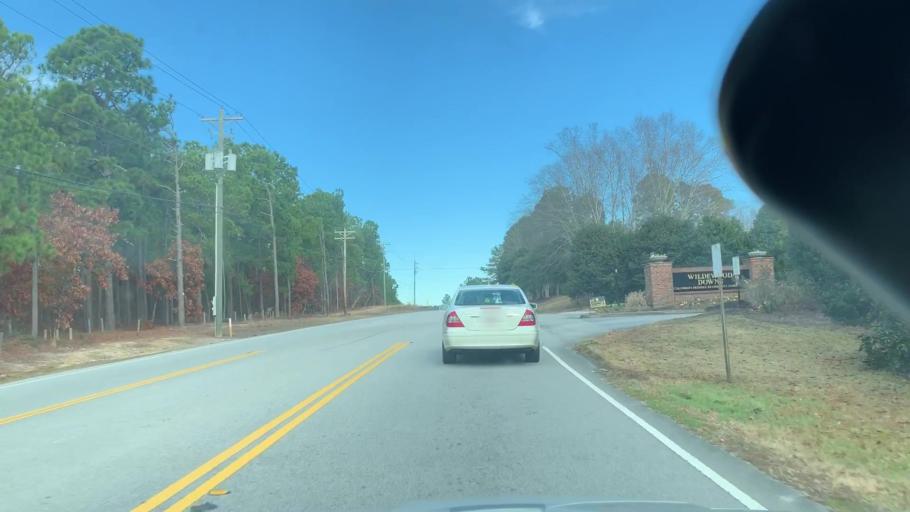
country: US
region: South Carolina
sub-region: Richland County
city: Woodfield
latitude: 34.0877
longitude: -80.8911
